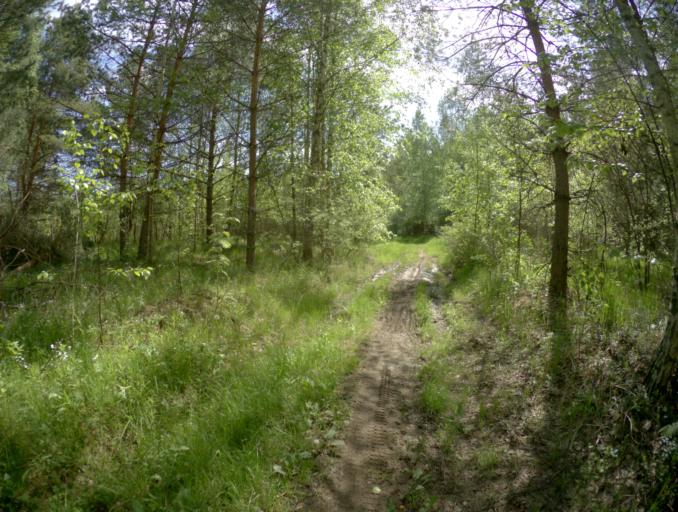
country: RU
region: Vladimir
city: Ivanishchi
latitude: 55.6675
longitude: 40.3880
